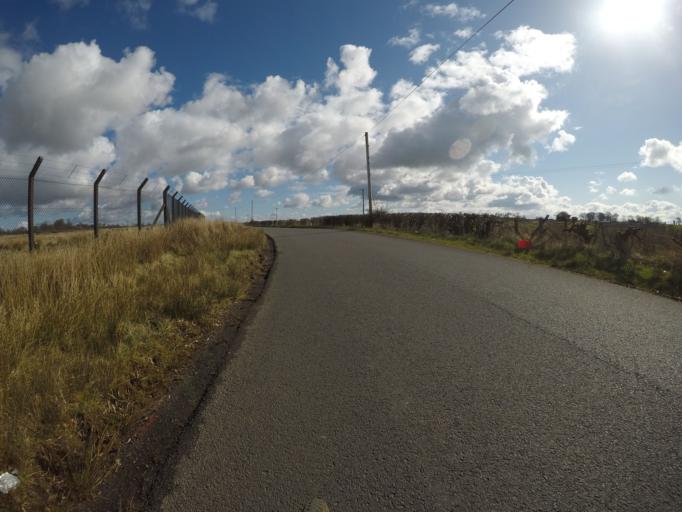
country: GB
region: Scotland
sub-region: North Ayrshire
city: Beith
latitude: 55.7227
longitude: -4.6111
